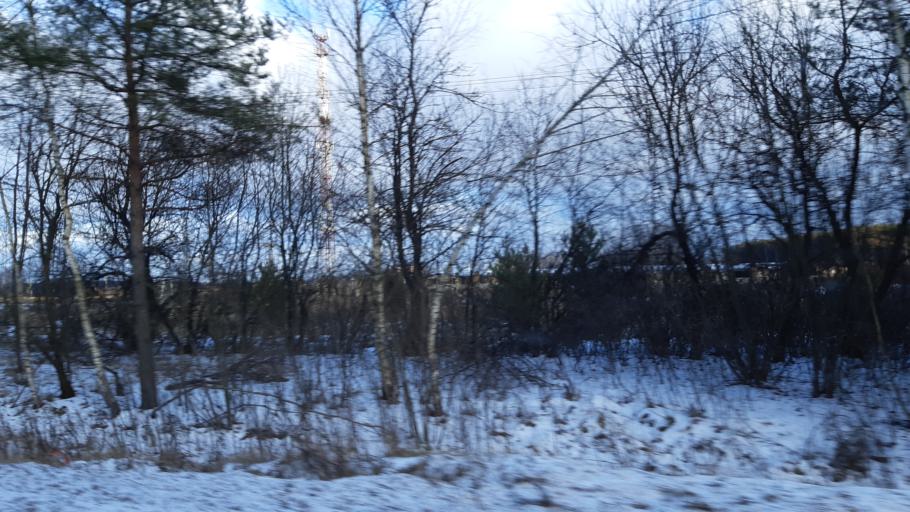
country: RU
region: Moskovskaya
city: Noginsk-9
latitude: 56.0479
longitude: 38.5516
